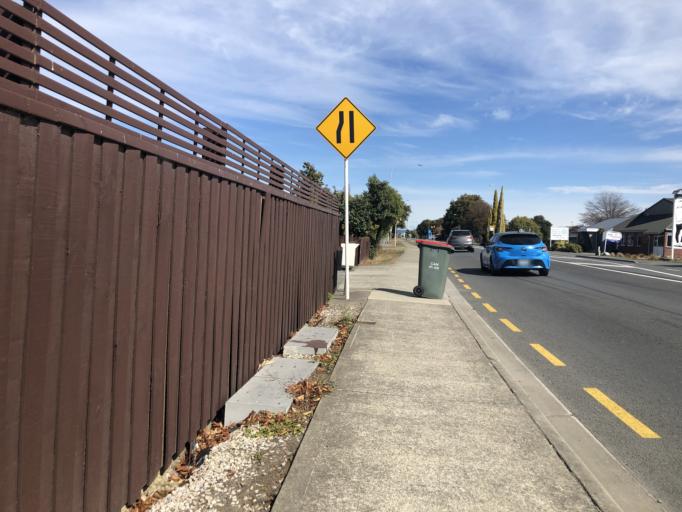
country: NZ
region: Tasman
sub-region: Tasman District
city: Richmond
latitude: -41.3377
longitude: 173.1801
